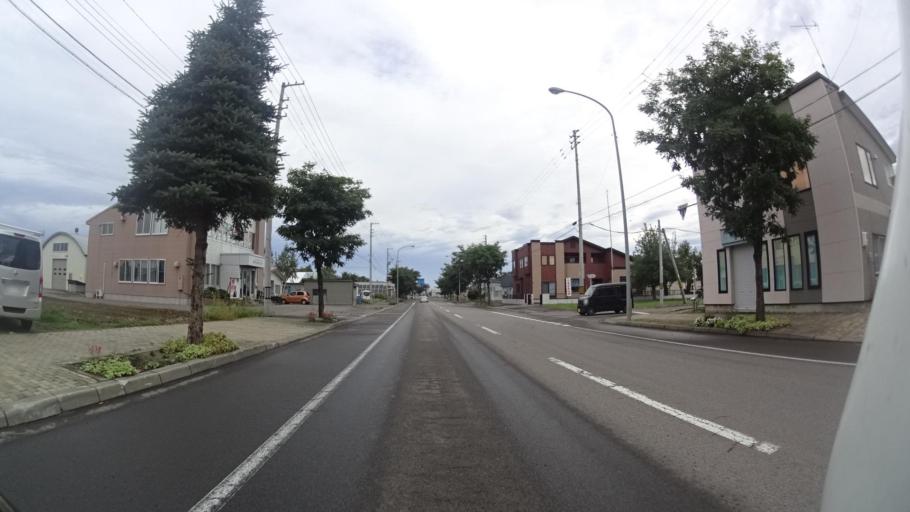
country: JP
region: Hokkaido
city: Abashiri
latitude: 43.8394
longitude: 144.5958
